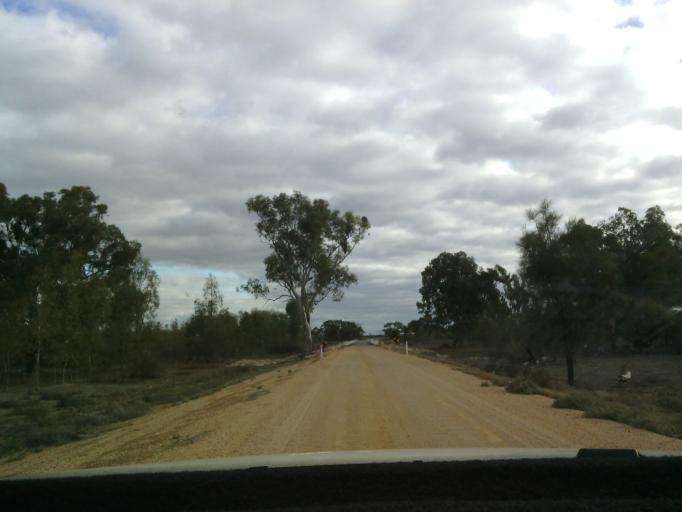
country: AU
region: South Australia
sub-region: Renmark Paringa
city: Renmark
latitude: -34.1674
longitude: 141.1853
